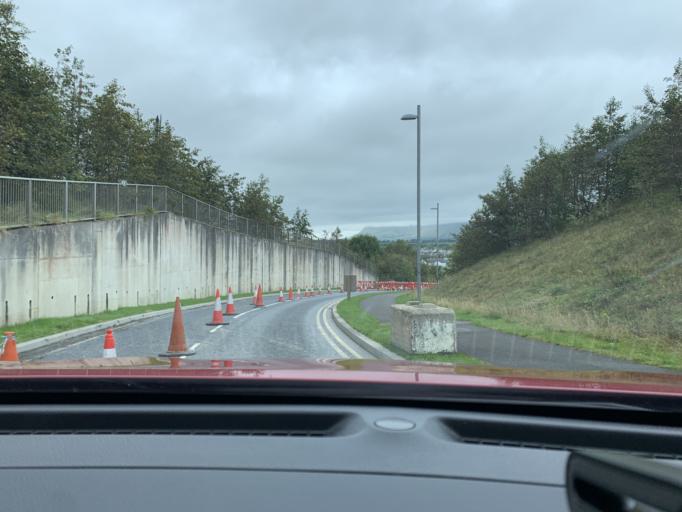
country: IE
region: Connaught
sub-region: Sligo
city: Sligo
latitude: 54.2754
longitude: -8.4664
